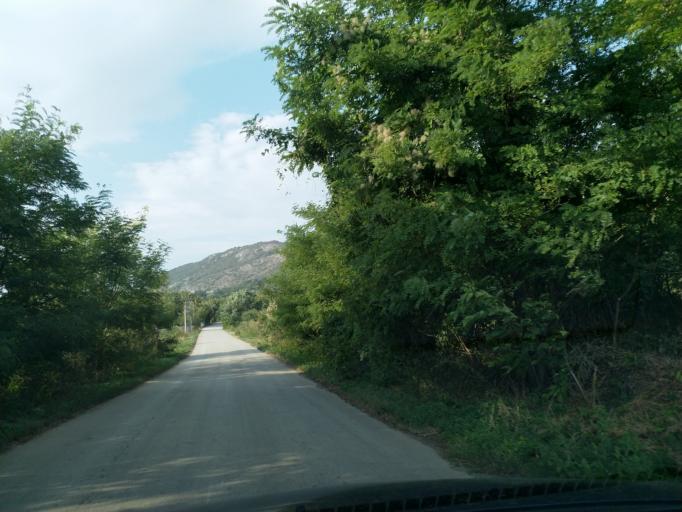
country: RS
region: Central Serbia
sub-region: Pomoravski Okrug
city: Paracin
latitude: 43.8283
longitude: 21.5419
